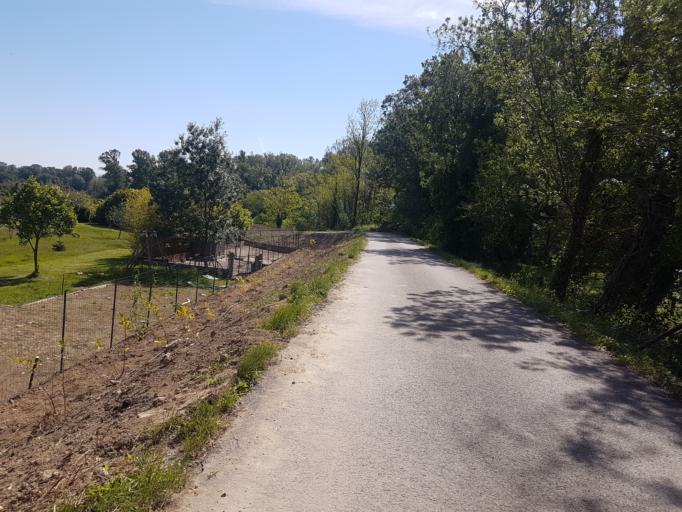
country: FR
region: Rhone-Alpes
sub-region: Departement de l'Ardeche
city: Le Pouzin
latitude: 44.7305
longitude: 4.7509
